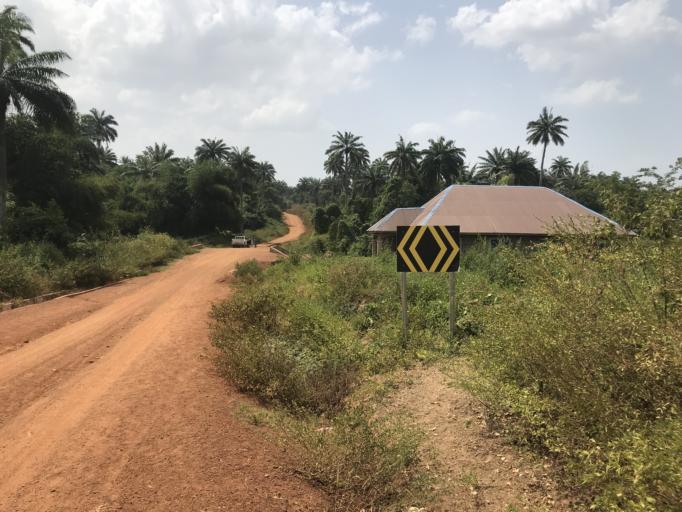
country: NG
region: Osun
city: Ikirun
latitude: 7.9349
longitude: 4.6372
